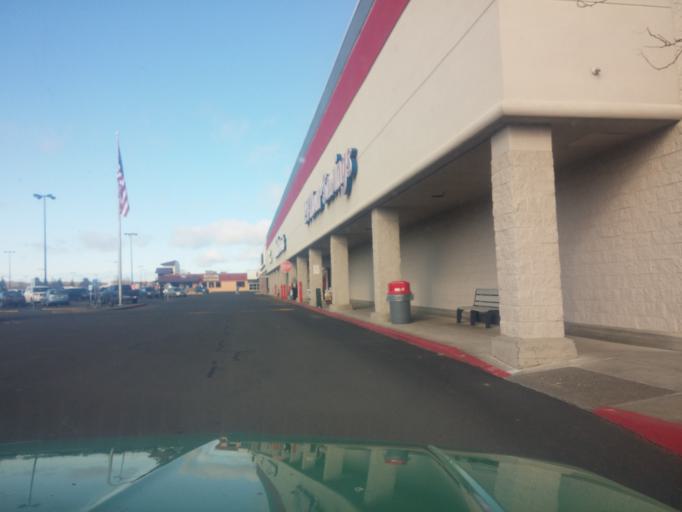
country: US
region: Idaho
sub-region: Latah County
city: Moscow
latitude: 46.7342
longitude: -117.0248
